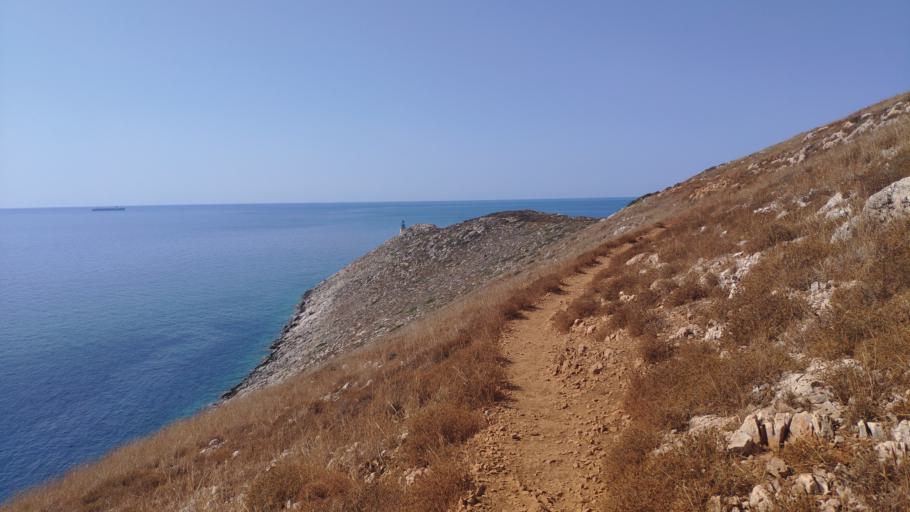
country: GR
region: Peloponnese
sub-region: Nomos Lakonias
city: Gytheio
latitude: 36.3911
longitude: 22.4835
